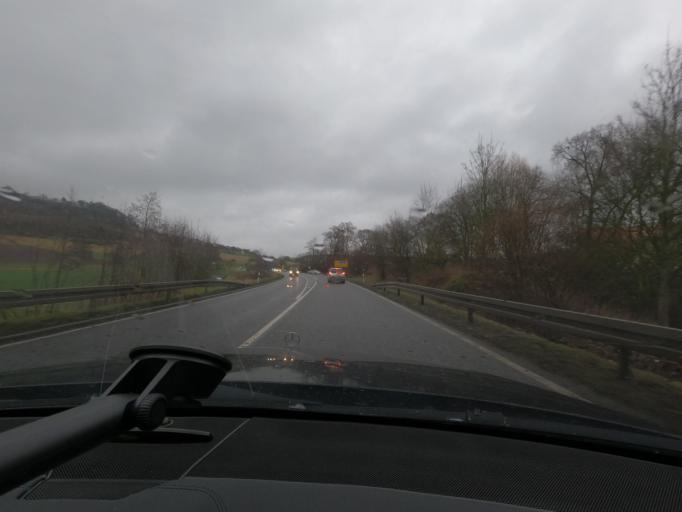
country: DE
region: Hesse
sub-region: Regierungsbezirk Kassel
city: Martinhagen
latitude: 51.3164
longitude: 9.2646
